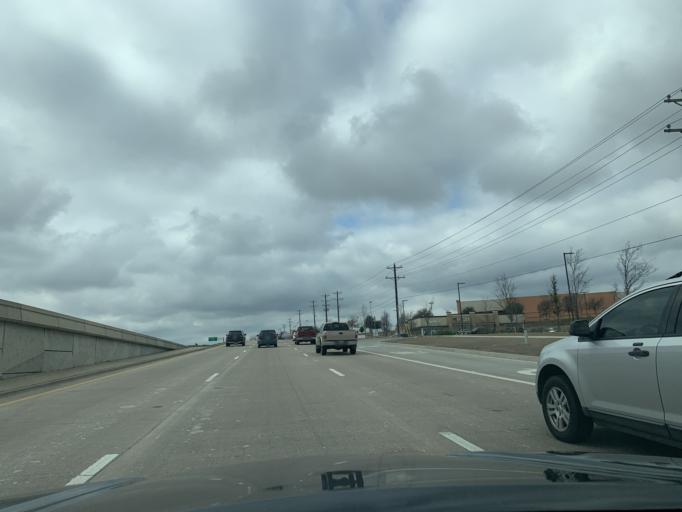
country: US
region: Texas
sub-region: Collin County
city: Allen
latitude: 33.1292
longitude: -96.7225
